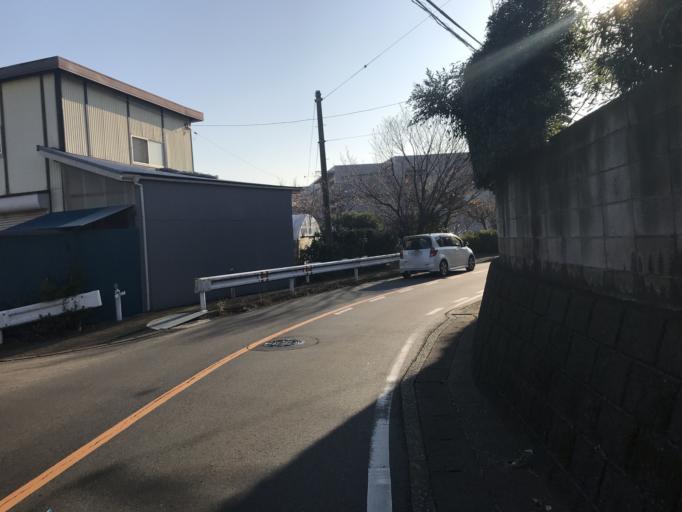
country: JP
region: Tokyo
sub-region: Machida-shi
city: Machida
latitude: 35.5588
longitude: 139.5218
